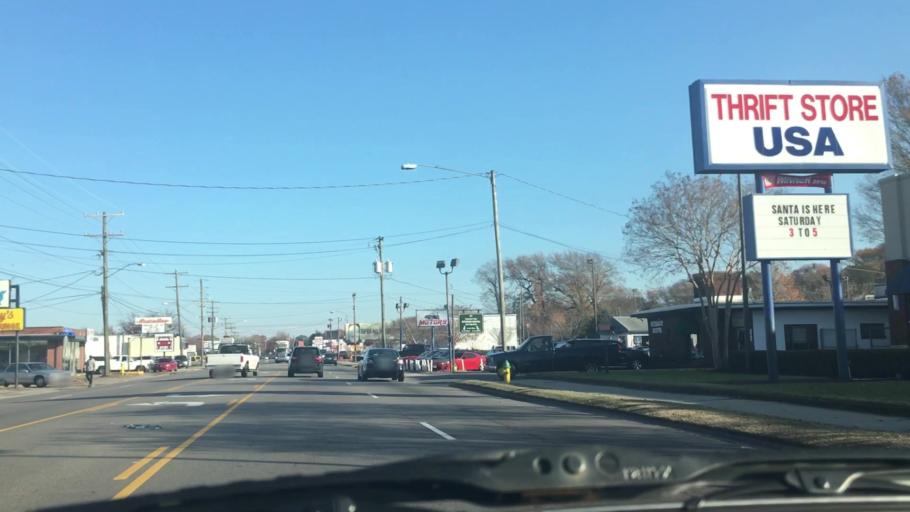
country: US
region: Virginia
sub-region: City of Norfolk
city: Norfolk
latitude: 36.9151
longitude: -76.2477
